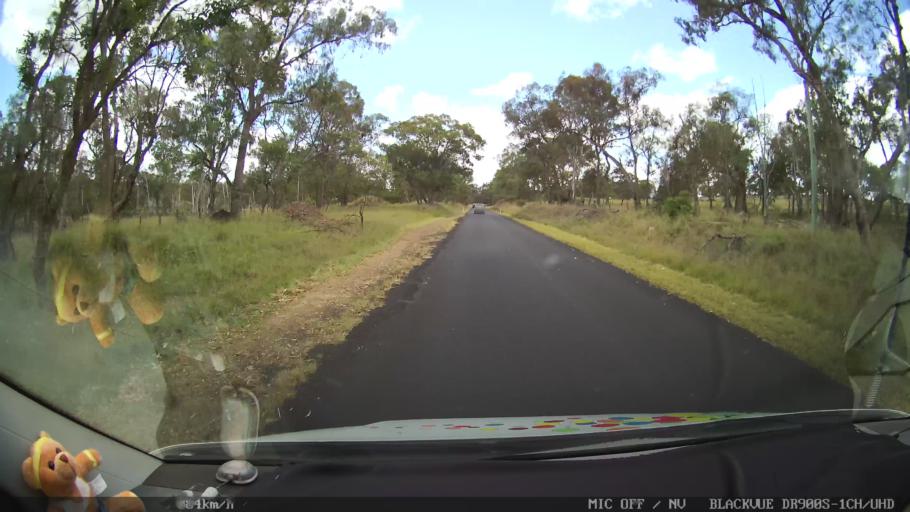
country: AU
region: New South Wales
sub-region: Glen Innes Severn
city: Glen Innes
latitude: -29.4295
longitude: 151.6575
